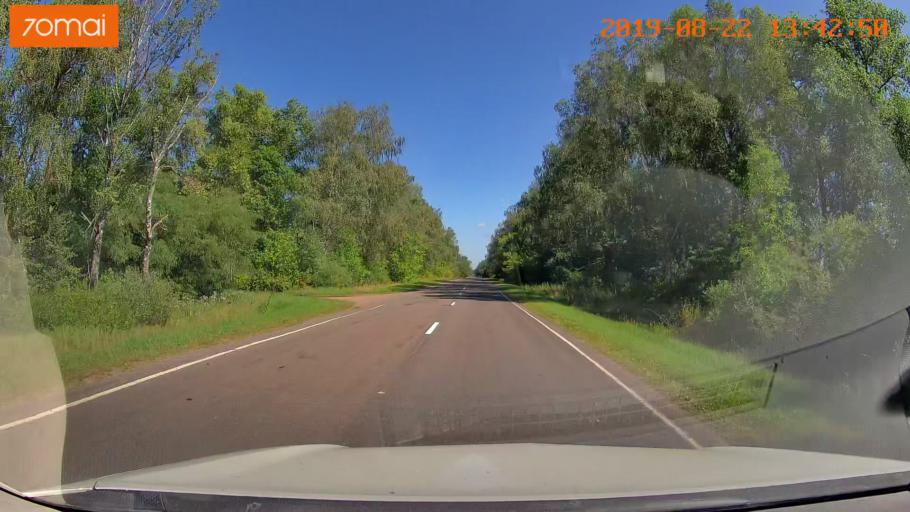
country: BY
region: Mogilev
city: Asipovichy
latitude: 53.2416
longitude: 28.4214
